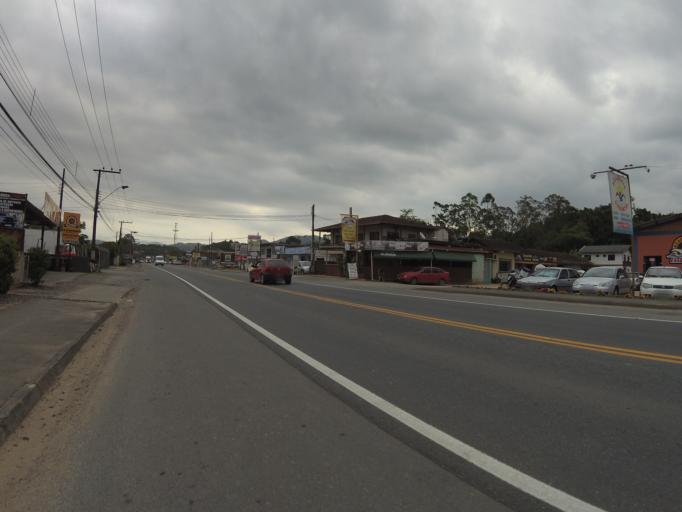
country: BR
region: Santa Catarina
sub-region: Blumenau
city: Blumenau
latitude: -26.8769
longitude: -49.1409
